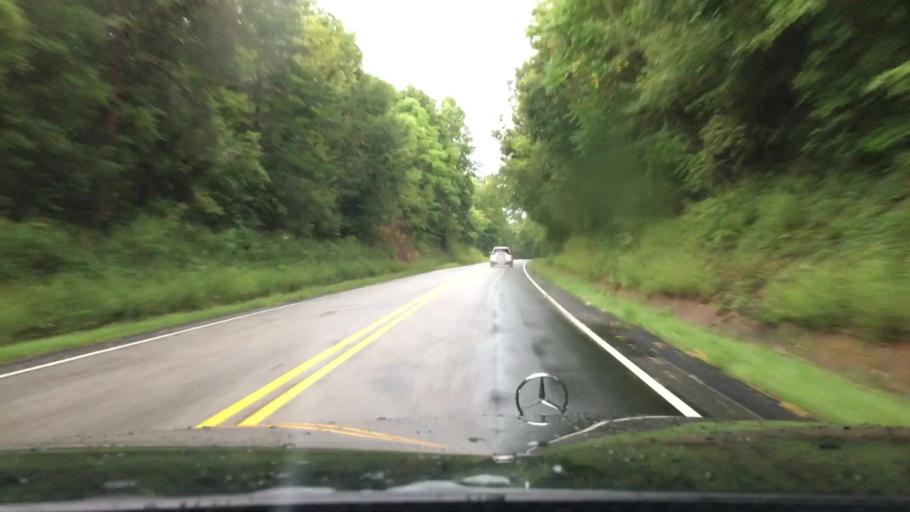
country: US
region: Virginia
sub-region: Amherst County
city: Amherst
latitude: 37.6892
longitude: -79.0259
